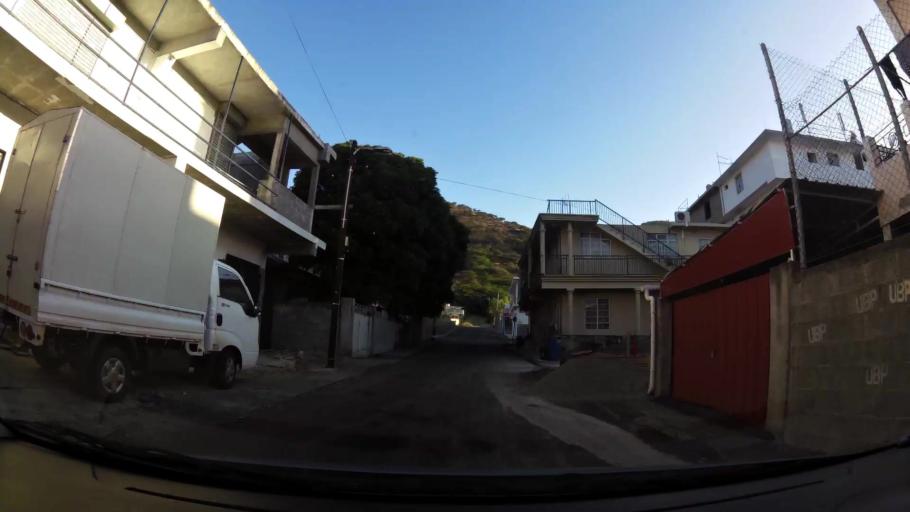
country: MU
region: Port Louis
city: Port Louis
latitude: -20.1749
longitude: 57.5073
